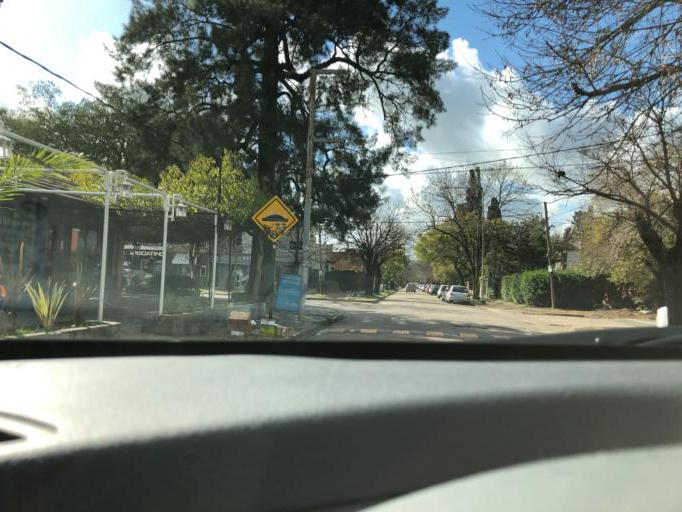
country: AR
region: Buenos Aires
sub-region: Partido de La Plata
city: La Plata
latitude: -34.8706
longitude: -58.0442
